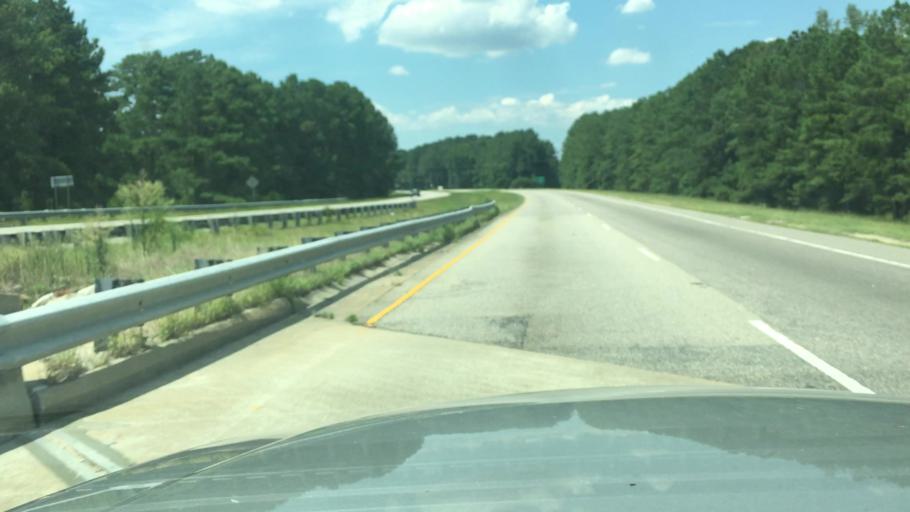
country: US
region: North Carolina
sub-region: Cumberland County
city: Vander
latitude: 34.9570
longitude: -78.8444
